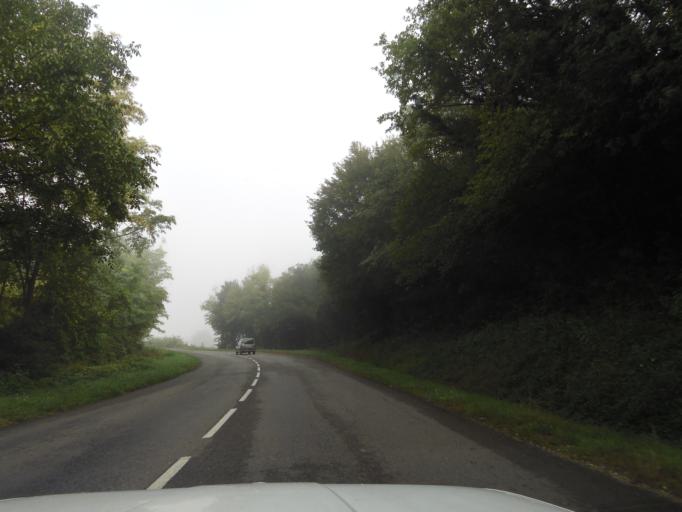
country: FR
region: Rhone-Alpes
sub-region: Departement de l'Isere
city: Creys-Mepieu
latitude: 45.7728
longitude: 5.4740
